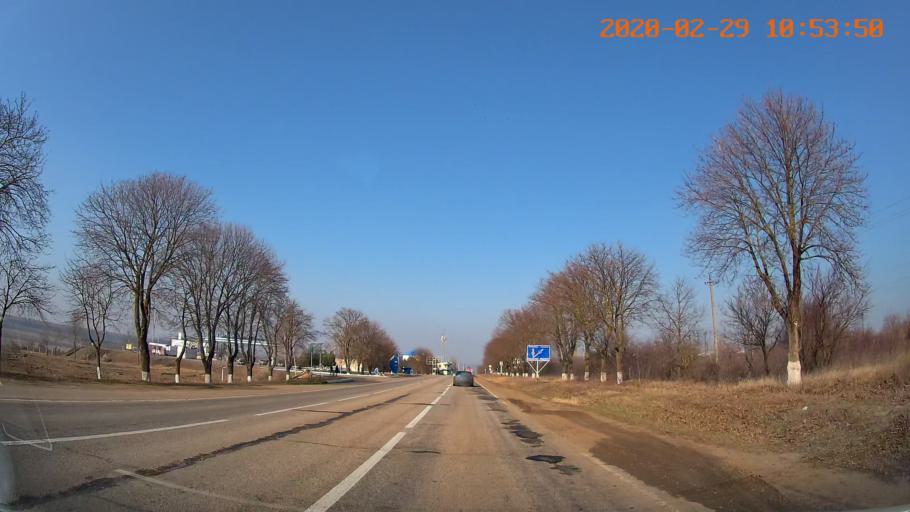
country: MD
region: Telenesti
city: Grigoriopol
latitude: 47.1187
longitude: 29.3306
